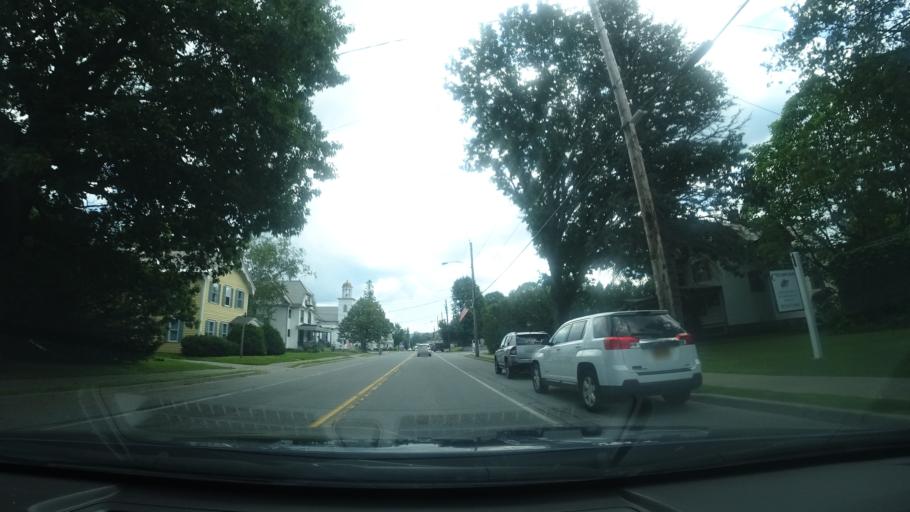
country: US
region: New York
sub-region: Warren County
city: Warrensburg
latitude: 43.4982
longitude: -73.7783
